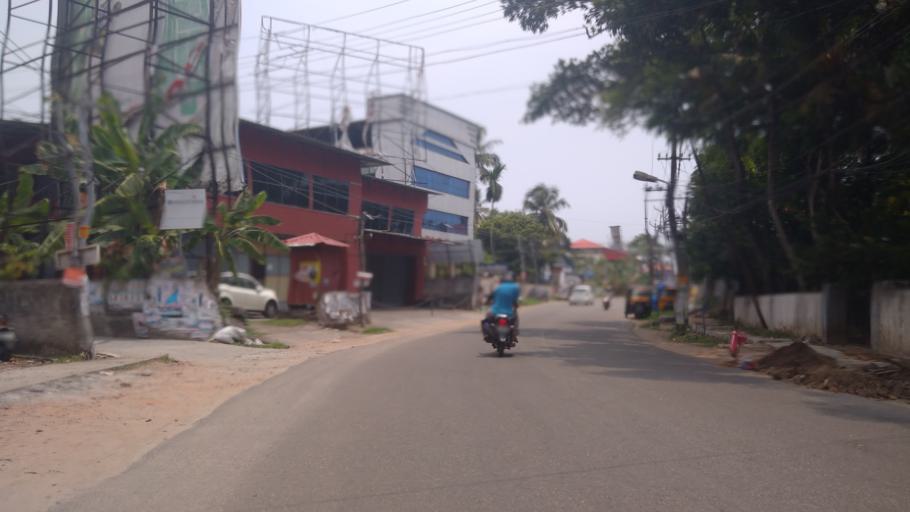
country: IN
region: Kerala
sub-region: Ernakulam
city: Elur
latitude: 10.0284
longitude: 76.3167
